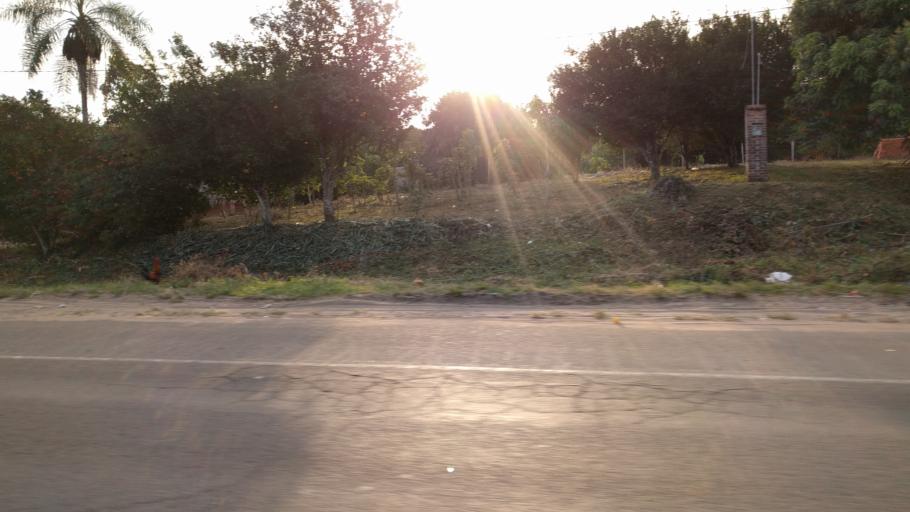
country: BO
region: Santa Cruz
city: Buena Vista
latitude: -17.4157
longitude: -63.6181
